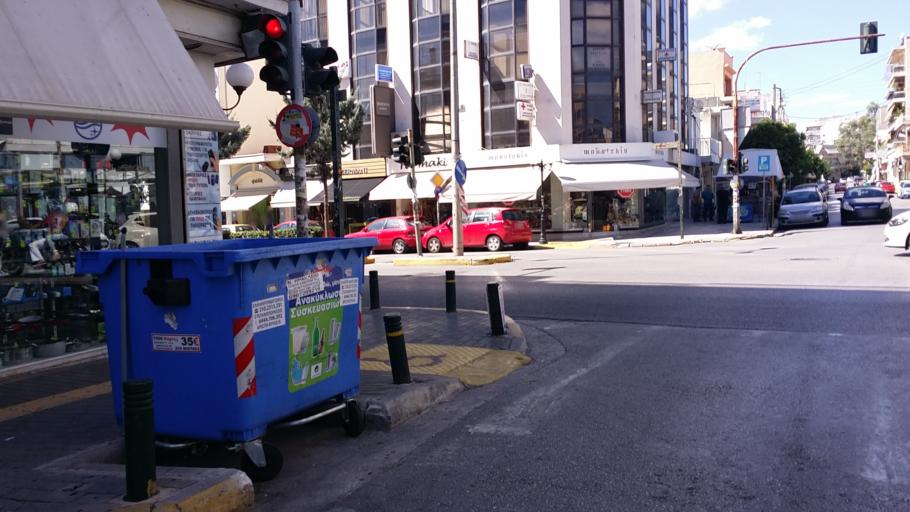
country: GR
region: Attica
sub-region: Nomarchia Athinas
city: Nea Ionia
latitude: 38.0443
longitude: 23.7555
